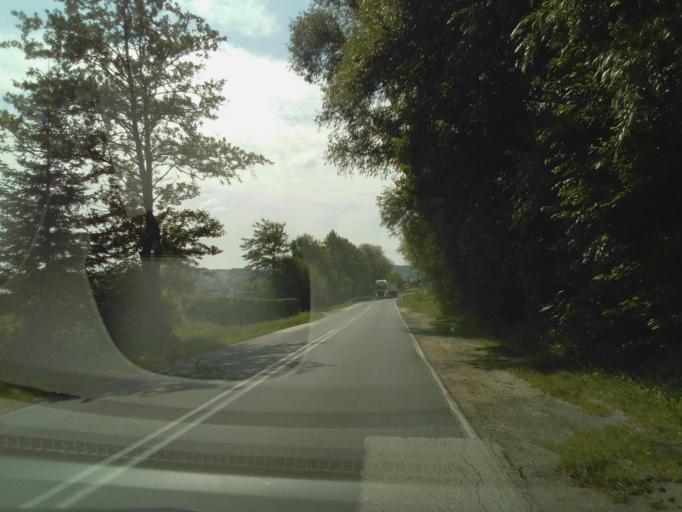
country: PL
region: Subcarpathian Voivodeship
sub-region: Powiat ropczycko-sedziszowski
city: Ropczyce
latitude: 50.0585
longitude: 21.5971
